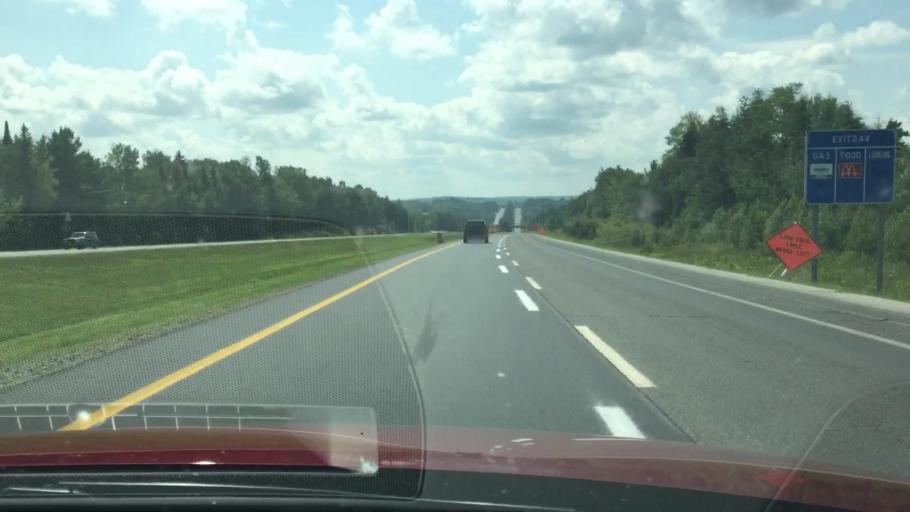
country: US
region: Maine
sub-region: Penobscot County
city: Medway
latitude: 45.6133
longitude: -68.5142
